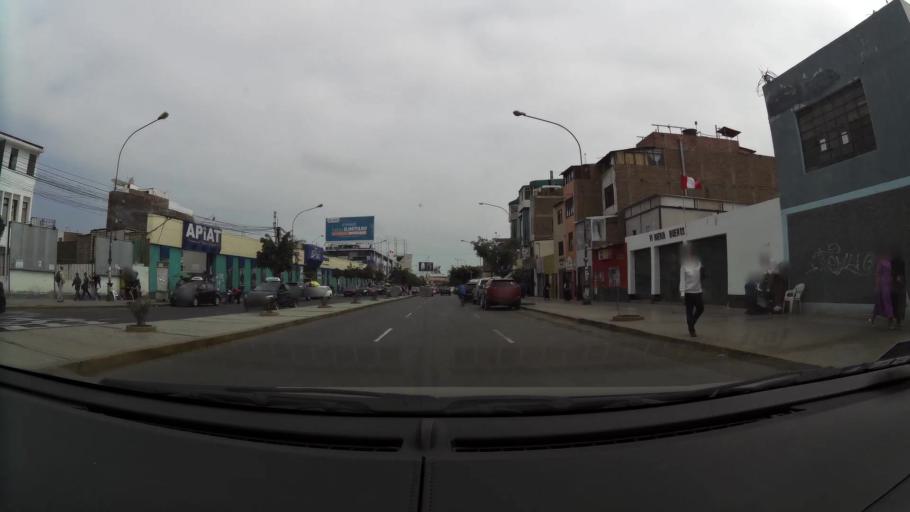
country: PE
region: La Libertad
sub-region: Provincia de Trujillo
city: Trujillo
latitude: -8.1111
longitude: -79.0223
